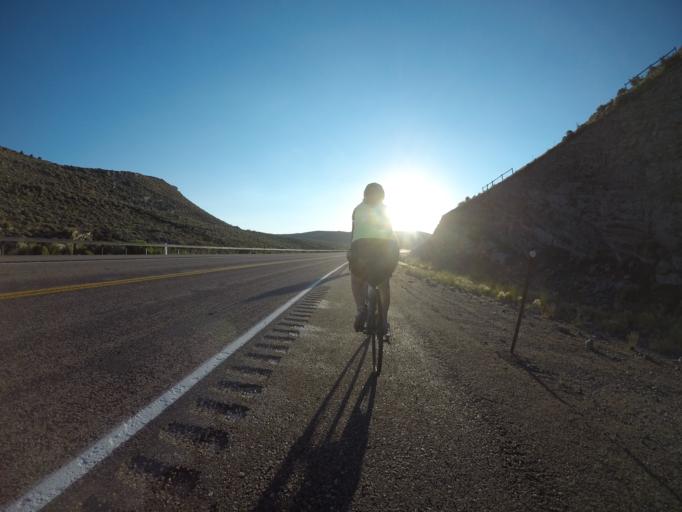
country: US
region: Wyoming
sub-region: Lincoln County
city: Kemmerer
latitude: 41.8715
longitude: -110.5240
